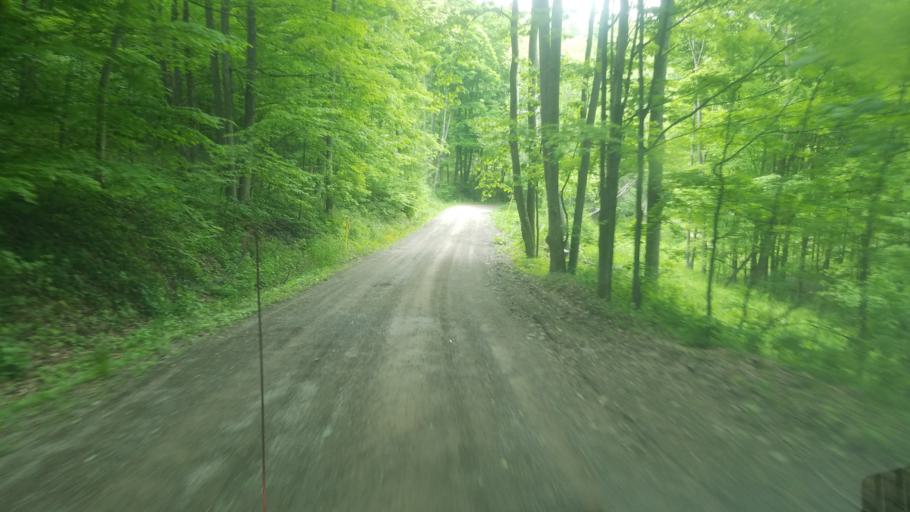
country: US
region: Pennsylvania
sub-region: Tioga County
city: Westfield
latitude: 41.9264
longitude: -77.7081
